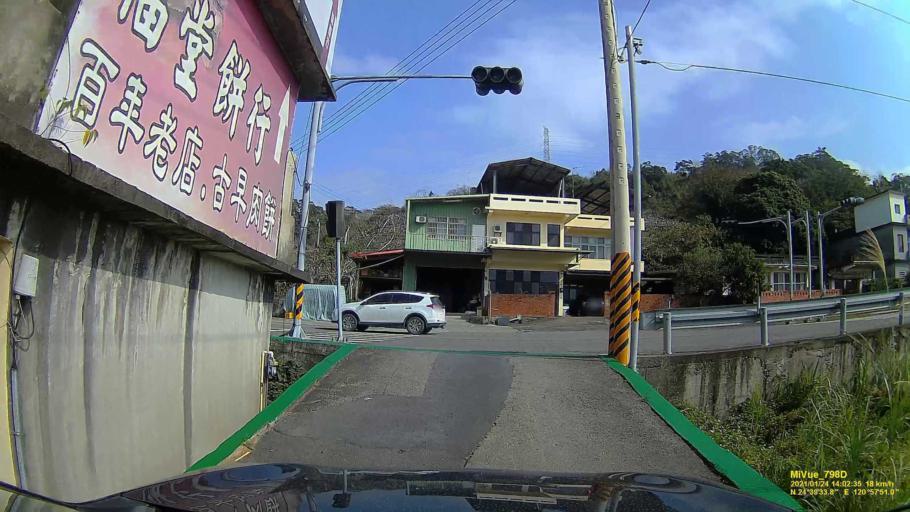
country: TW
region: Taiwan
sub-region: Hsinchu
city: Hsinchu
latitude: 24.6594
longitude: 120.9643
